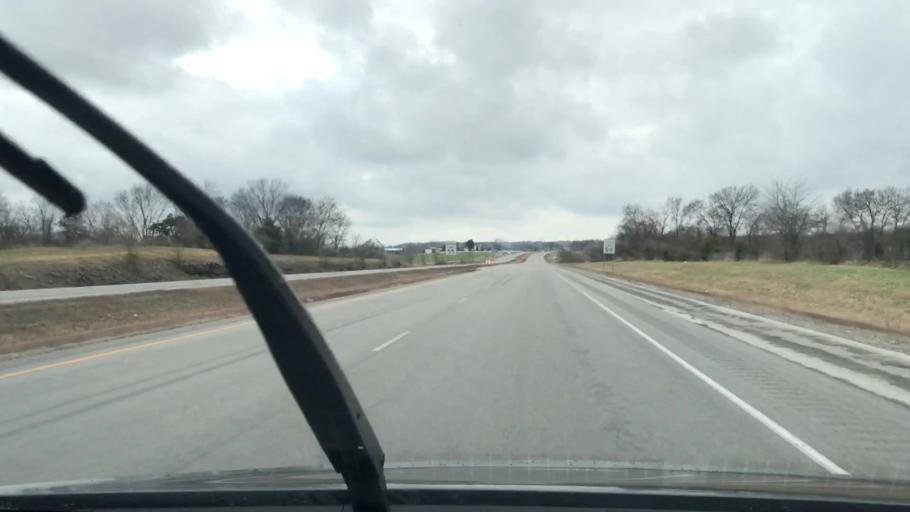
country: US
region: Kentucky
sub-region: Christian County
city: Hopkinsville
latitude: 36.8547
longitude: -87.4120
